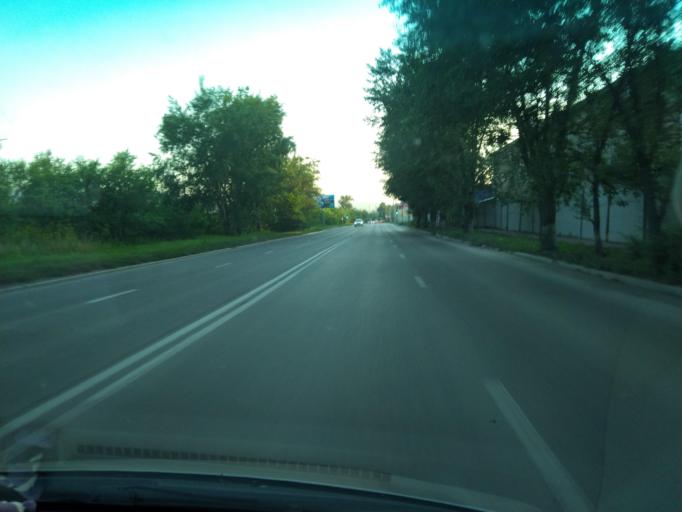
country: RU
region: Krasnoyarskiy
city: Krasnoyarsk
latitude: 55.9906
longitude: 92.9152
